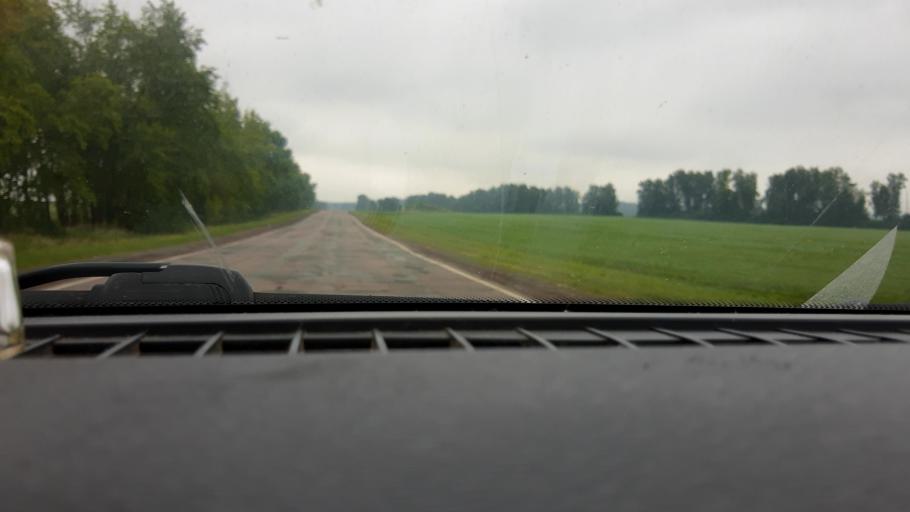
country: RU
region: Bashkortostan
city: Belebey
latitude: 54.2940
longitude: 54.0619
